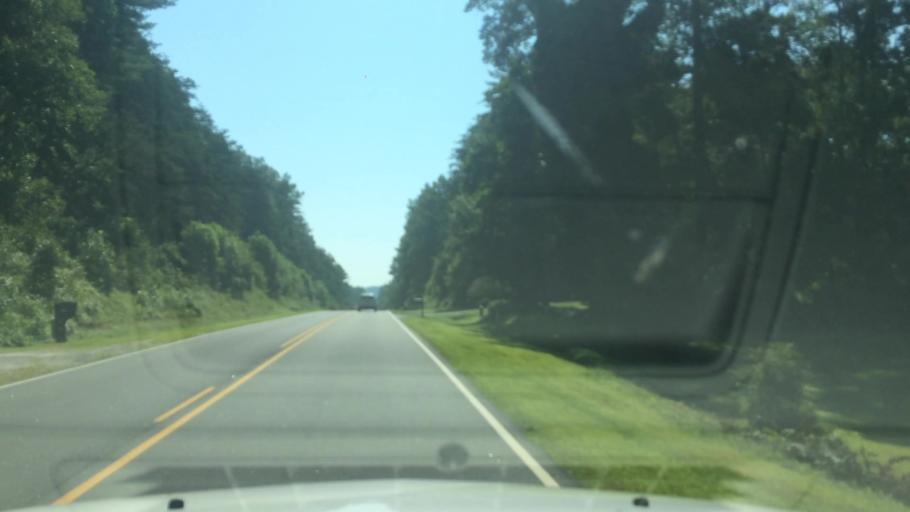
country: US
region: North Carolina
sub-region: Caldwell County
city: Hudson
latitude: 35.9088
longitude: -81.4209
